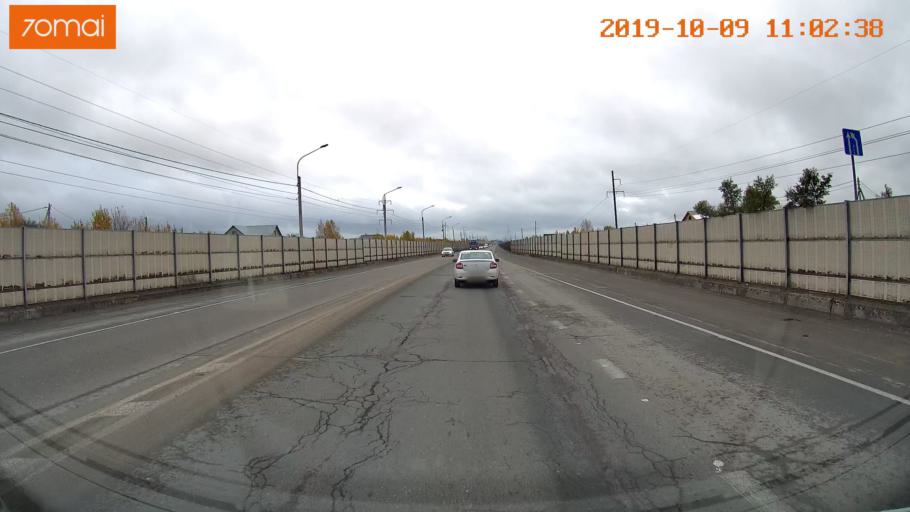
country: RU
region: Vologda
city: Vologda
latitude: 59.2290
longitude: 39.7750
